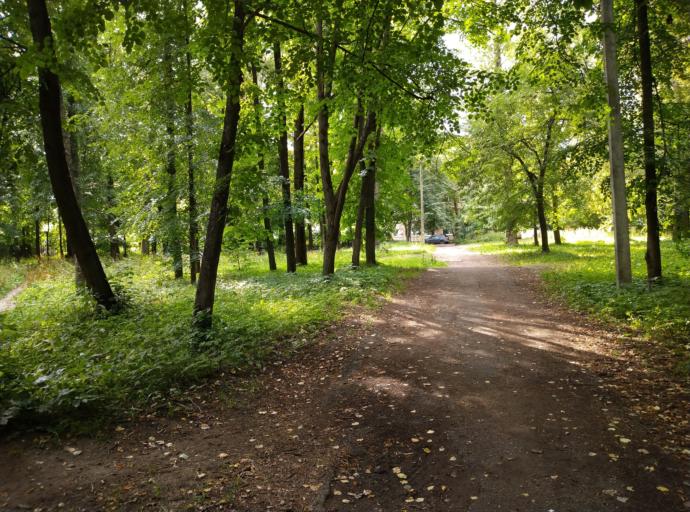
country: RU
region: Kostroma
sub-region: Kostromskoy Rayon
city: Kostroma
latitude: 57.7540
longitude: 40.9562
